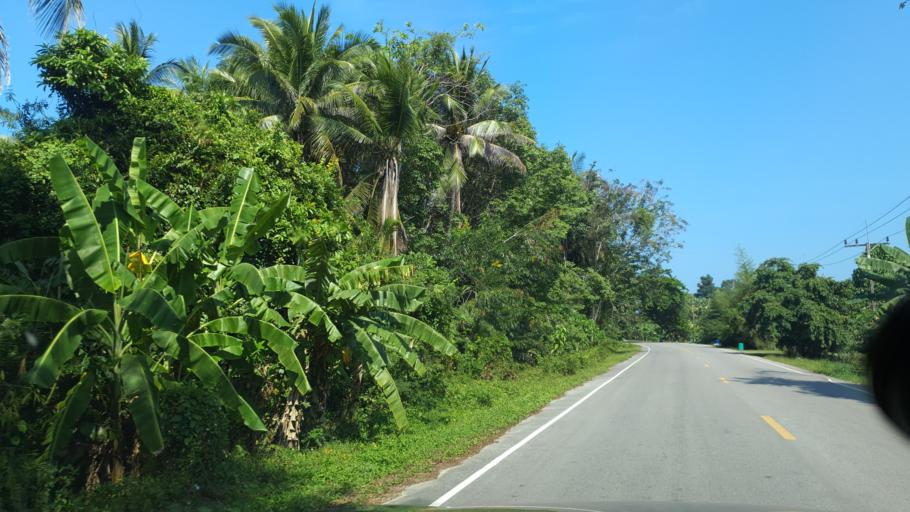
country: TH
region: Surat Thani
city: Tha Chana
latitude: 9.5839
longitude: 99.1978
